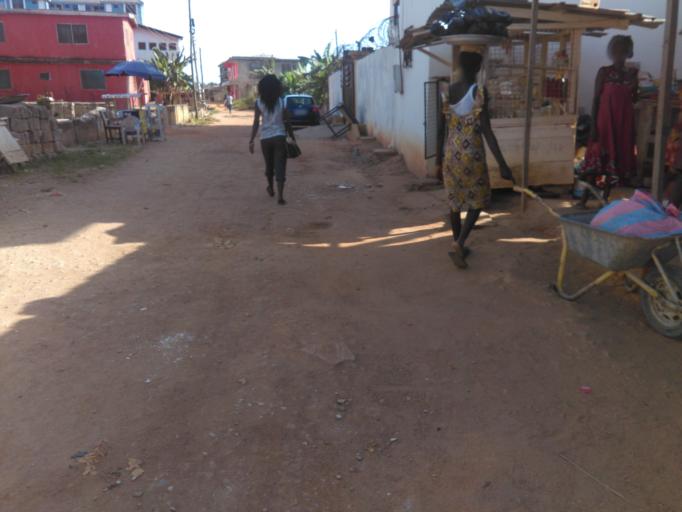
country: GH
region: Central
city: Cape Coast
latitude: 5.1153
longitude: -1.2981
